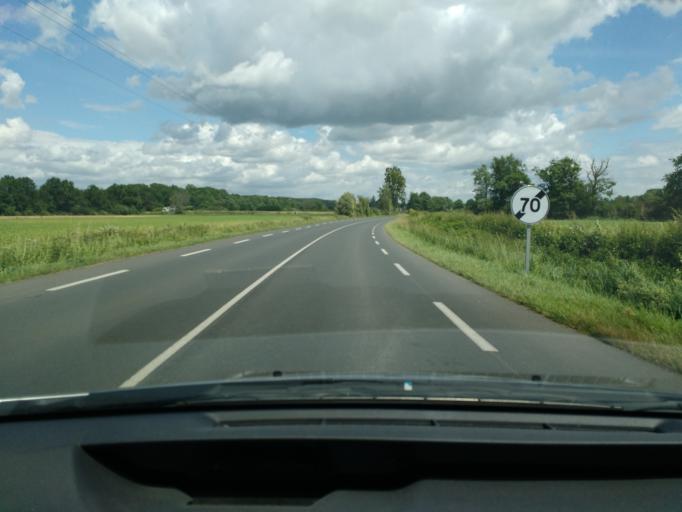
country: FR
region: Pays de la Loire
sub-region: Departement de Maine-et-Loire
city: Le Plessis-Grammoire
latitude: 47.4896
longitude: -0.4648
